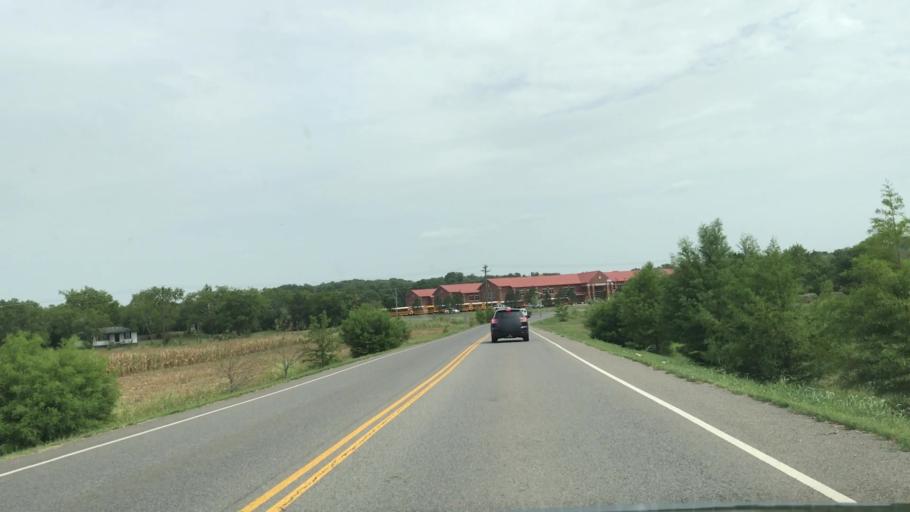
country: US
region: Tennessee
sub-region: Williamson County
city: Nolensville
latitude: 35.9517
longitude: -86.6640
